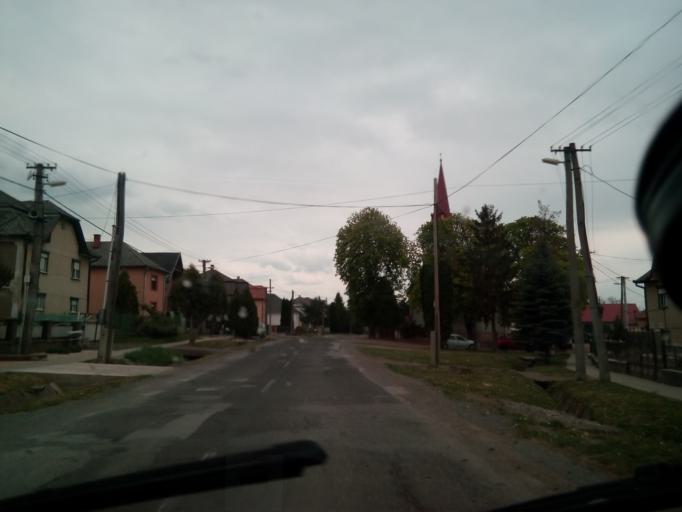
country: SK
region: Kosicky
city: Kosice
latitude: 48.7428
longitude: 21.4393
